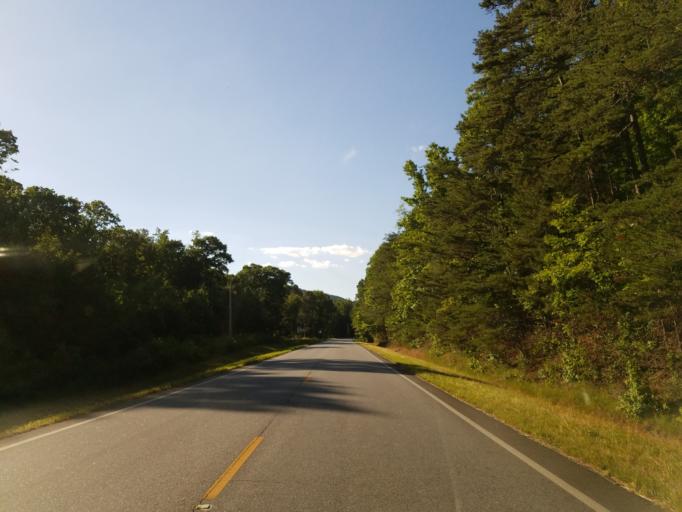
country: US
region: Georgia
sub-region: Gordon County
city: Calhoun
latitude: 34.6211
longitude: -85.0544
